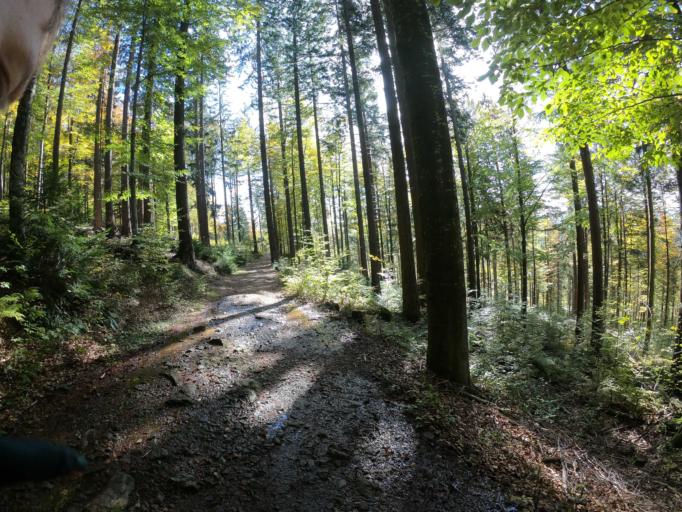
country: DE
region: Bavaria
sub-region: Lower Bavaria
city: Bodenmais
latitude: 49.0833
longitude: 13.1150
